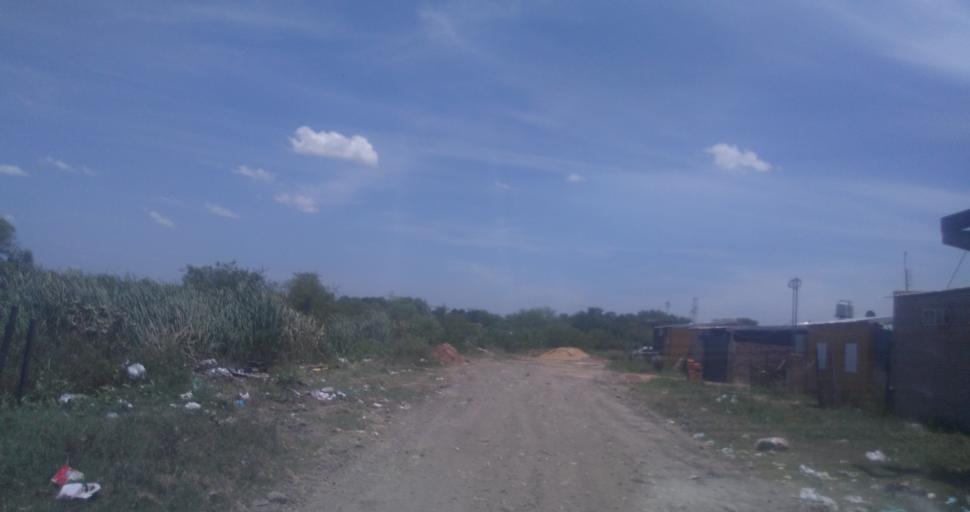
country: AR
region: Chaco
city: Fontana
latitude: -27.4240
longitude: -59.0415
